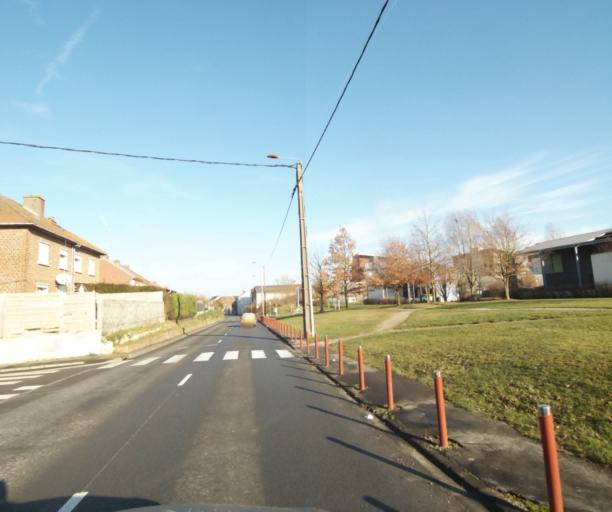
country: FR
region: Nord-Pas-de-Calais
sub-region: Departement du Nord
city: Valenciennes
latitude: 50.3454
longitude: 3.5323
